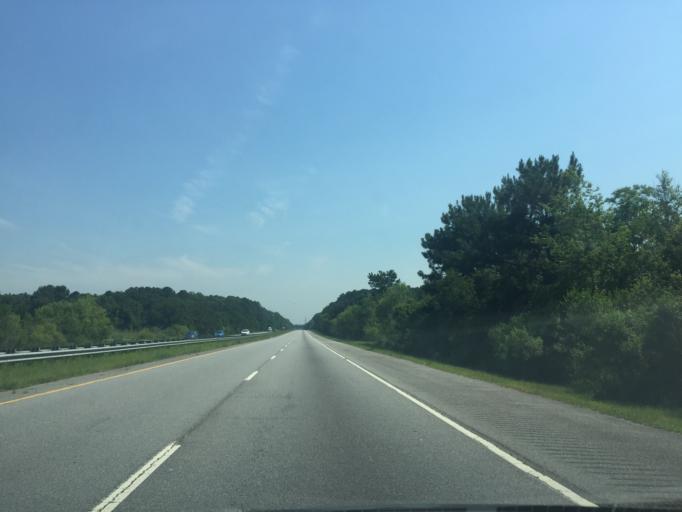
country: US
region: Georgia
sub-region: Chatham County
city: Georgetown
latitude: 32.0191
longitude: -81.1737
